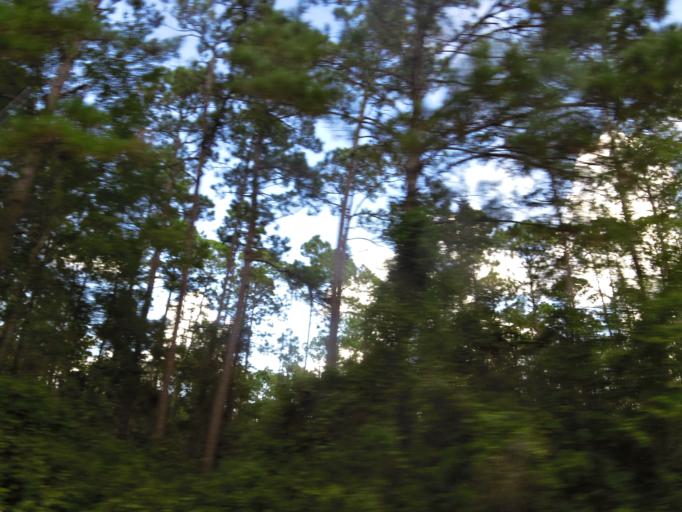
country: US
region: Georgia
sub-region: Echols County
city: Statenville
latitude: 30.7475
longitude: -83.1061
